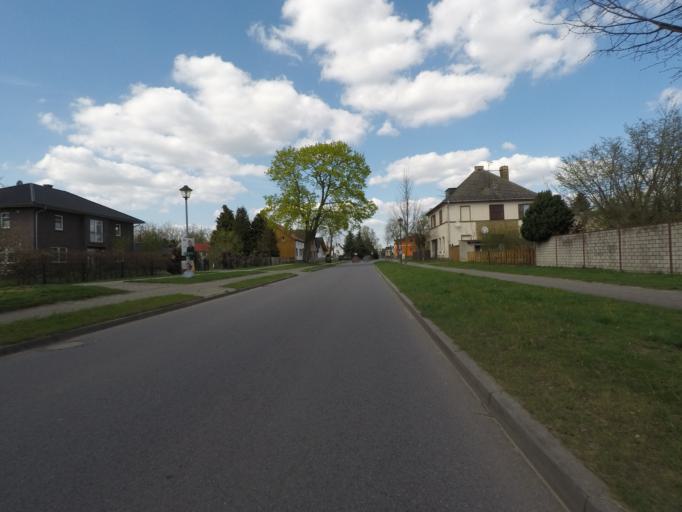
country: DE
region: Brandenburg
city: Melchow
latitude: 52.8521
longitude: 13.6821
